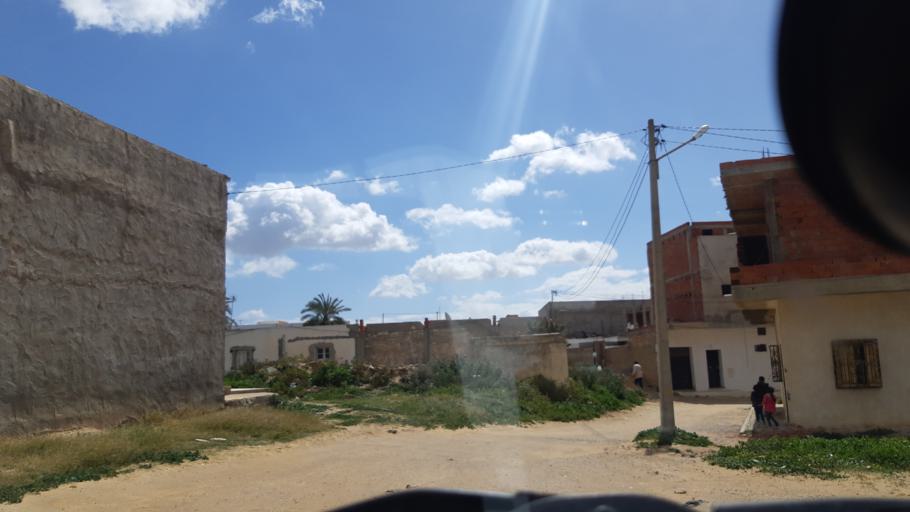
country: TN
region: Susah
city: Akouda
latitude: 35.8798
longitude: 10.5336
